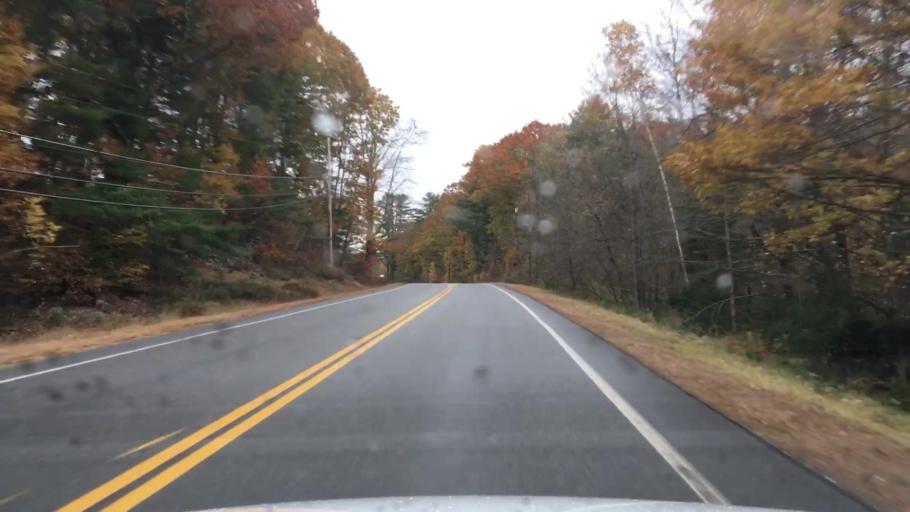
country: US
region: Maine
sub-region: Lincoln County
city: Jefferson
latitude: 44.2021
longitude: -69.4993
